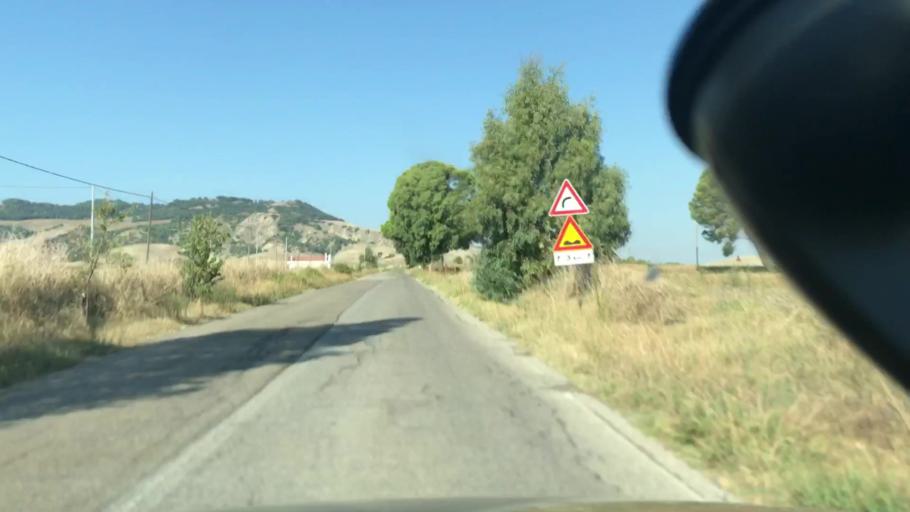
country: IT
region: Basilicate
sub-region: Provincia di Matera
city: La Martella
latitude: 40.6584
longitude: 16.5201
